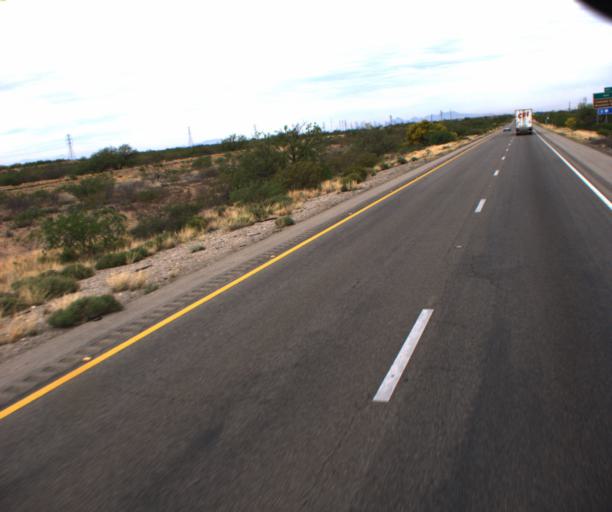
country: US
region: Arizona
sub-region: Pima County
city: Vail
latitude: 32.0212
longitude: -110.7104
